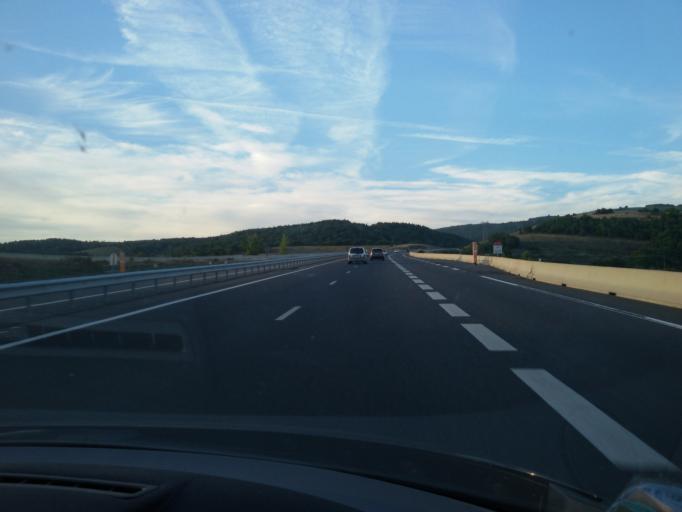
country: FR
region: Midi-Pyrenees
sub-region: Departement de l'Aveyron
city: Millau
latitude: 44.2045
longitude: 3.0675
